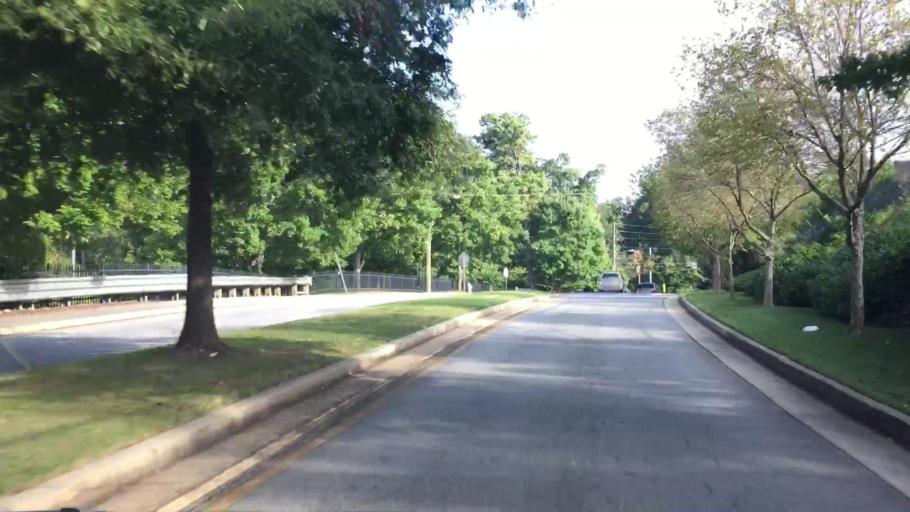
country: US
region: Georgia
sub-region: DeKalb County
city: Decatur
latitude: 33.7461
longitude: -84.3144
